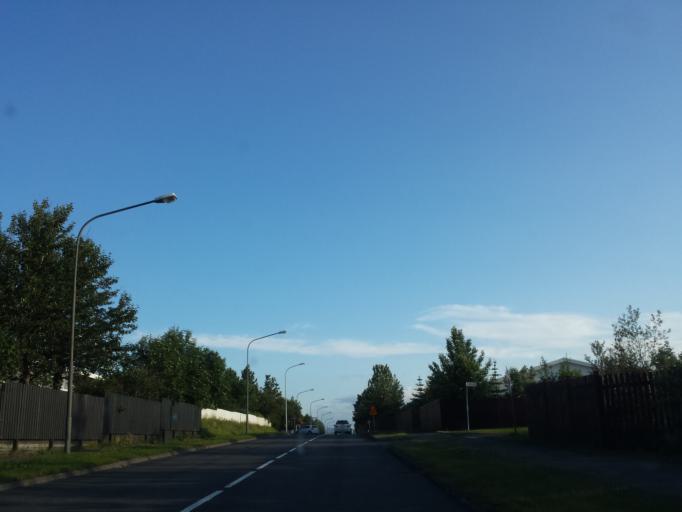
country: IS
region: Capital Region
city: Mosfellsbaer
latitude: 64.1108
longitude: -21.7864
